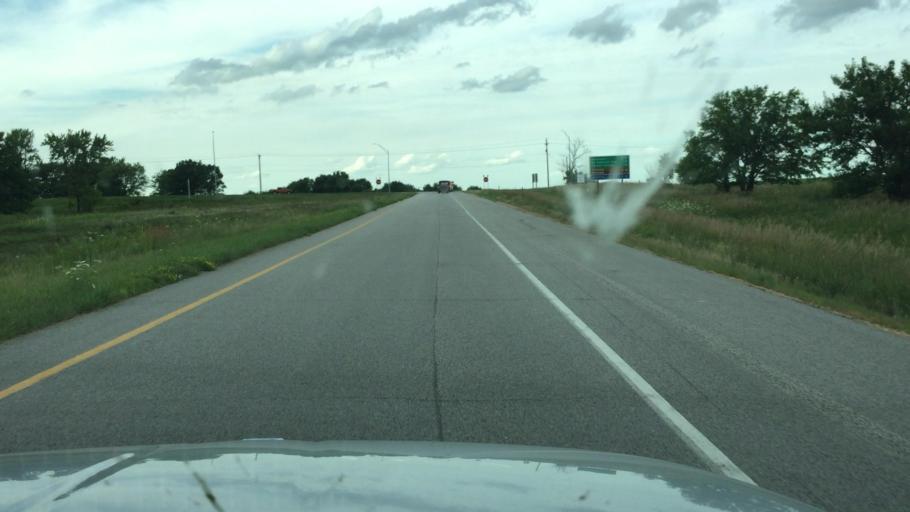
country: US
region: Iowa
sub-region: Scott County
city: Buffalo
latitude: 41.5362
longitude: -90.6753
